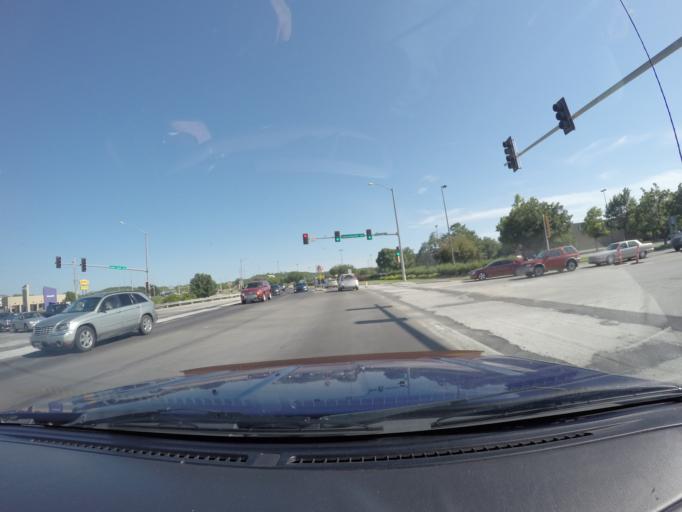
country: US
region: Kansas
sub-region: Riley County
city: Manhattan
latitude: 39.1816
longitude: -96.5583
